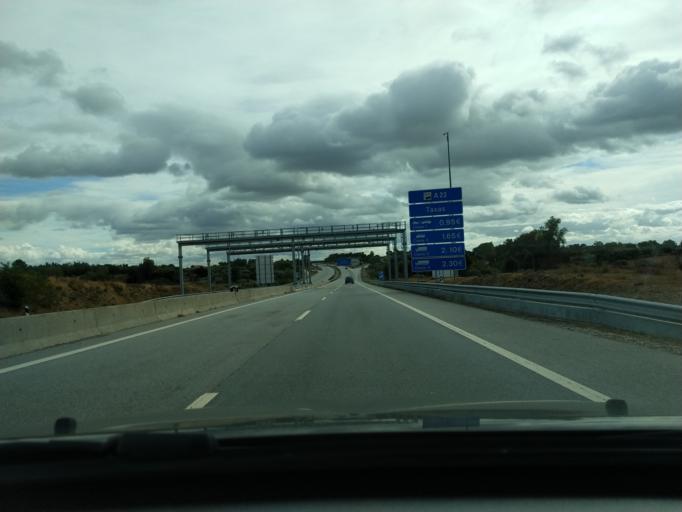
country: PT
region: Castelo Branco
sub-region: Concelho do Fundao
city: Fundao
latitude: 40.0340
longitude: -7.4687
